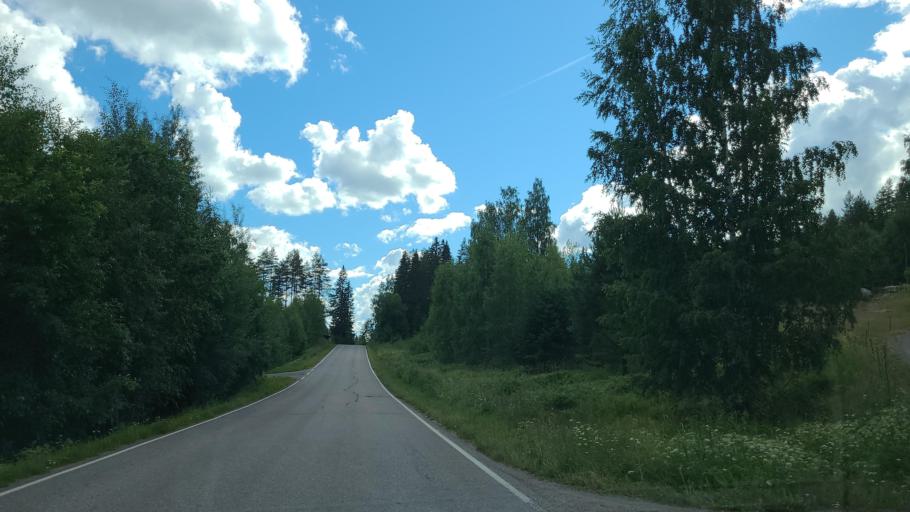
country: FI
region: Central Finland
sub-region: Jaemsae
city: Jaemsae
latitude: 61.8882
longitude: 25.2475
